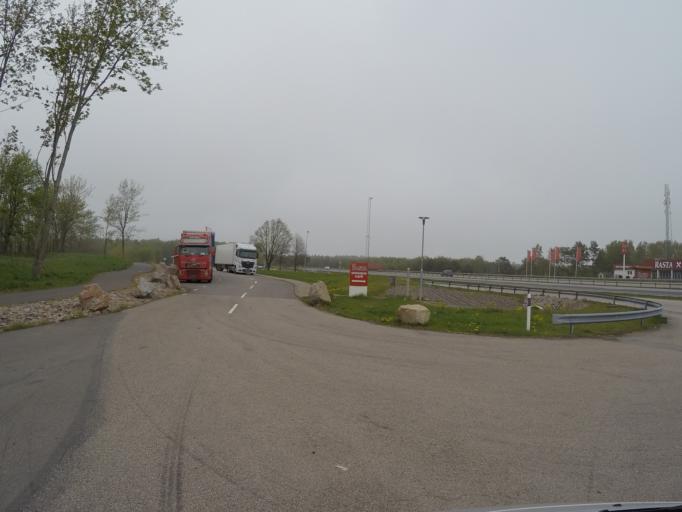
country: SE
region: Halland
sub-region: Laholms Kommun
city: Mellbystrand
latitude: 56.5414
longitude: 12.9690
